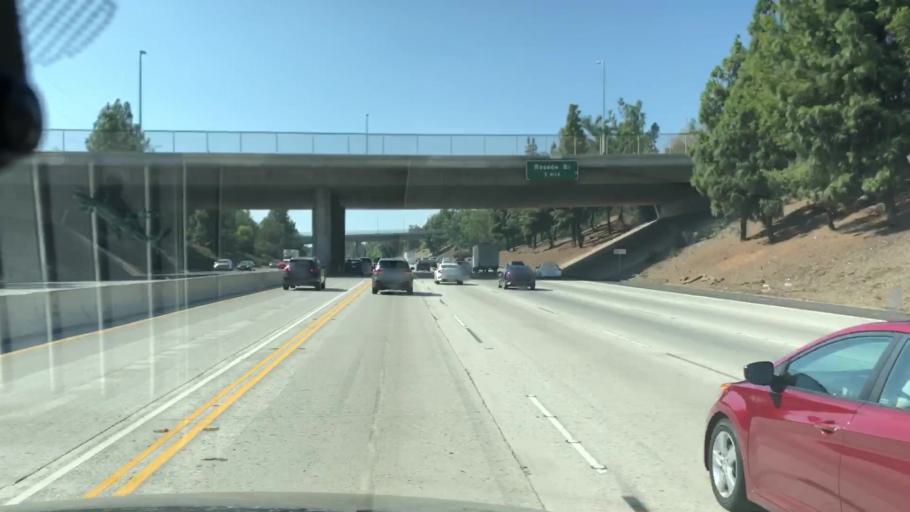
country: US
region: California
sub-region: Los Angeles County
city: Northridge
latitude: 34.2785
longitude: -118.5188
